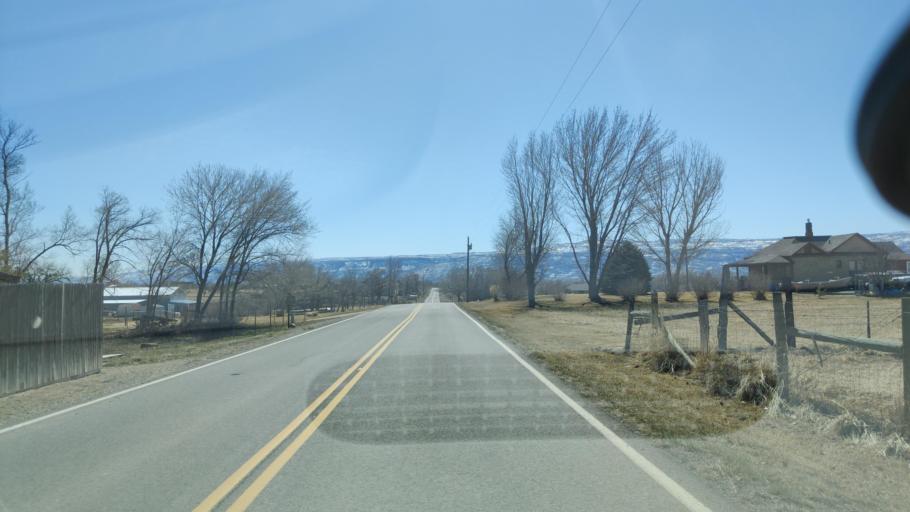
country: US
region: Colorado
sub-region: Mesa County
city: Fruita
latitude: 39.1808
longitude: -108.7105
